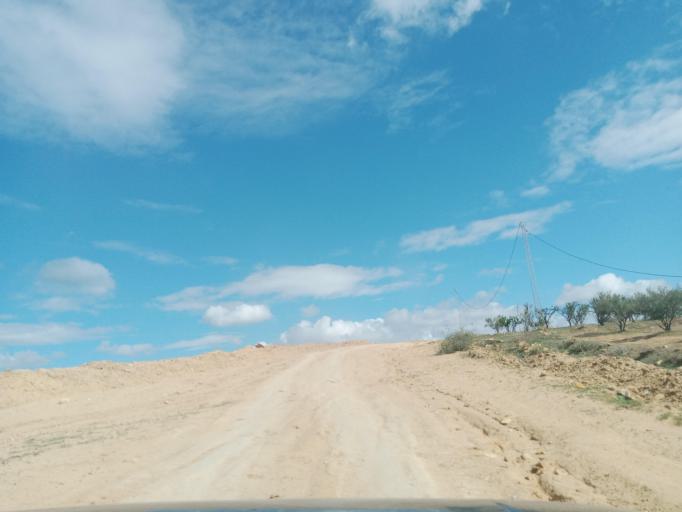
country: TN
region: Tunis
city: Oued Lill
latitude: 36.8078
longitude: 9.9874
